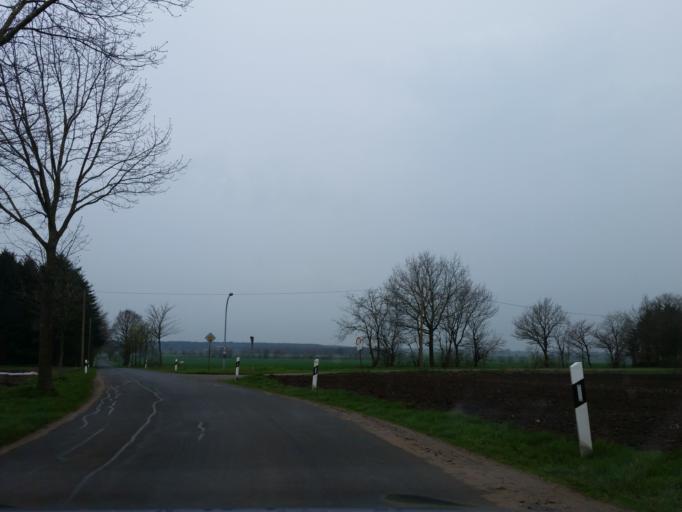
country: DE
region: Lower Saxony
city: Alfstedt
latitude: 53.5730
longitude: 9.0698
